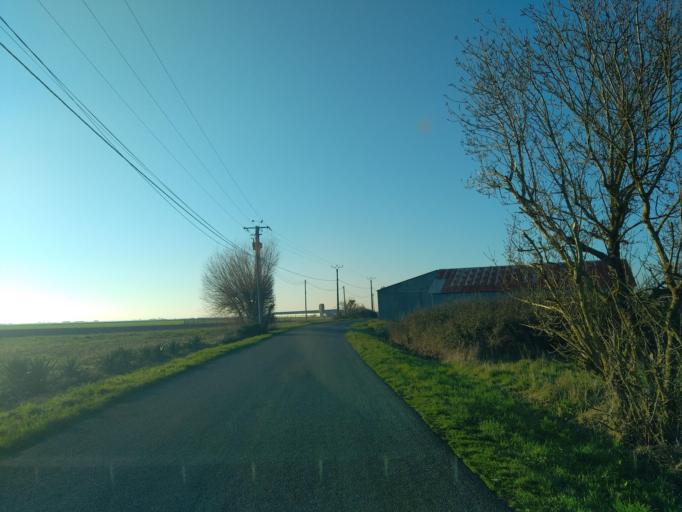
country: FR
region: Pays de la Loire
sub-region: Departement de la Vendee
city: Triaize
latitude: 46.3884
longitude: -1.2730
